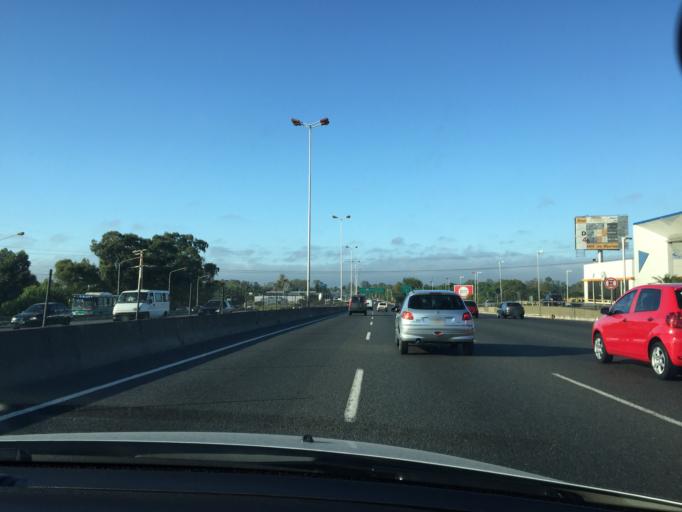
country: AR
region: Buenos Aires F.D.
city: Villa Lugano
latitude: -34.7115
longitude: -58.5057
